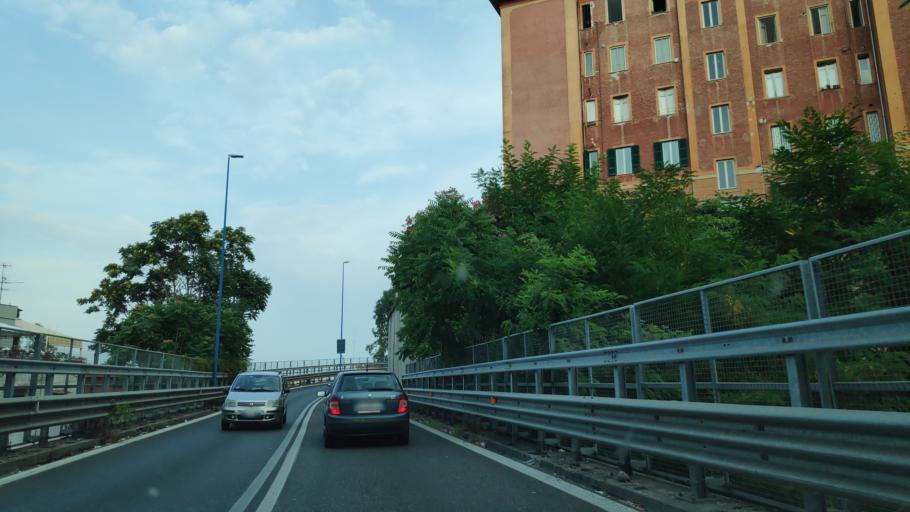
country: IT
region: Campania
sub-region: Provincia di Napoli
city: Napoli
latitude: 40.8564
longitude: 14.2330
